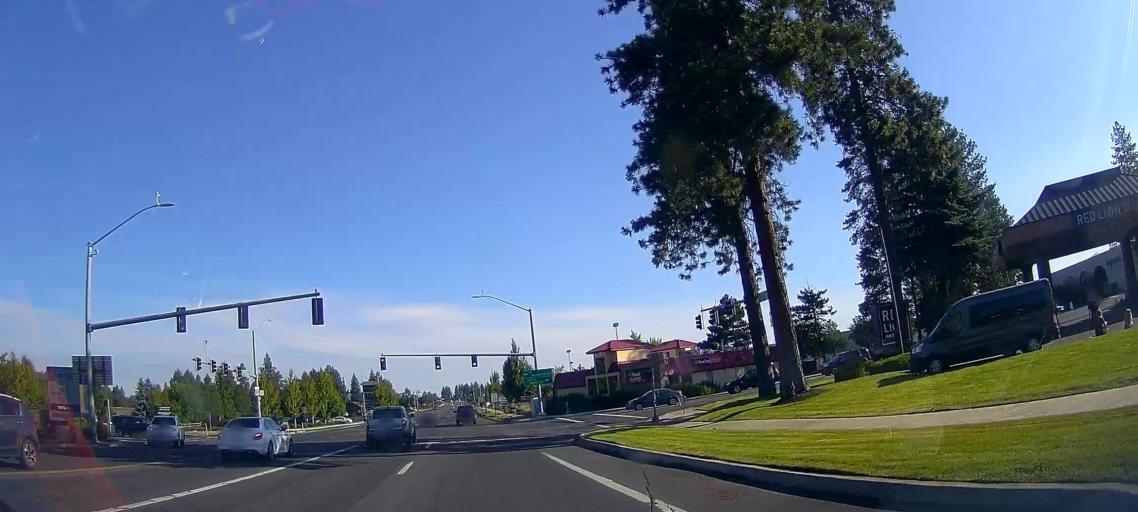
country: US
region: Oregon
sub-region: Deschutes County
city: Bend
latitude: 44.0789
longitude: -121.3047
